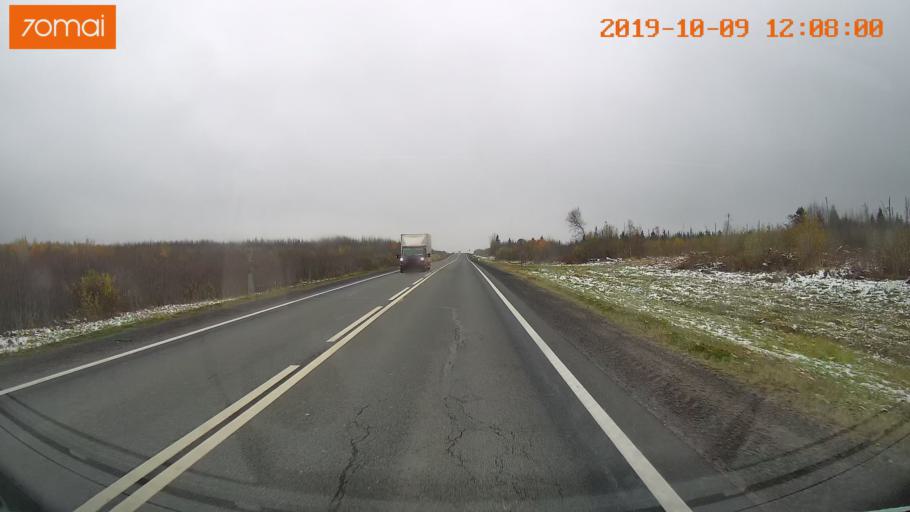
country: RU
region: Jaroslavl
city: Prechistoye
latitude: 58.5924
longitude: 40.3454
